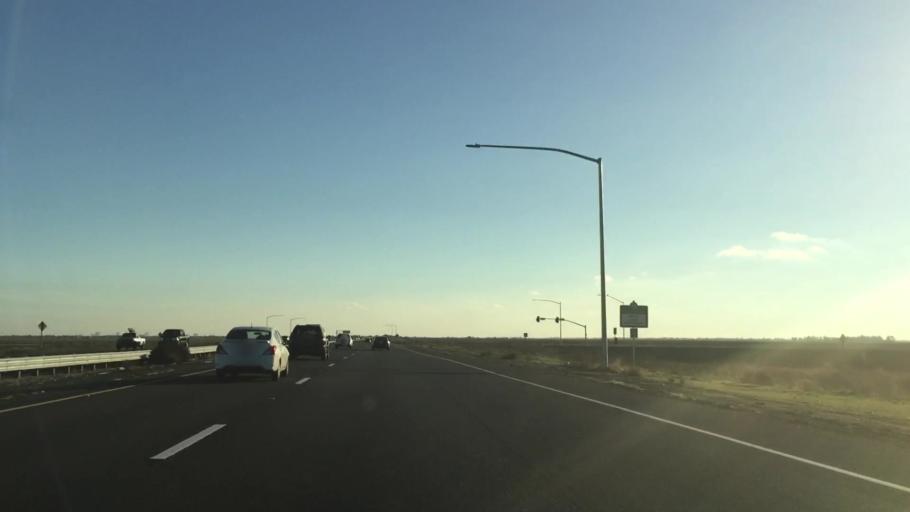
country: US
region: California
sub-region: Sacramento County
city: Elverta
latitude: 38.7128
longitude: -121.5405
